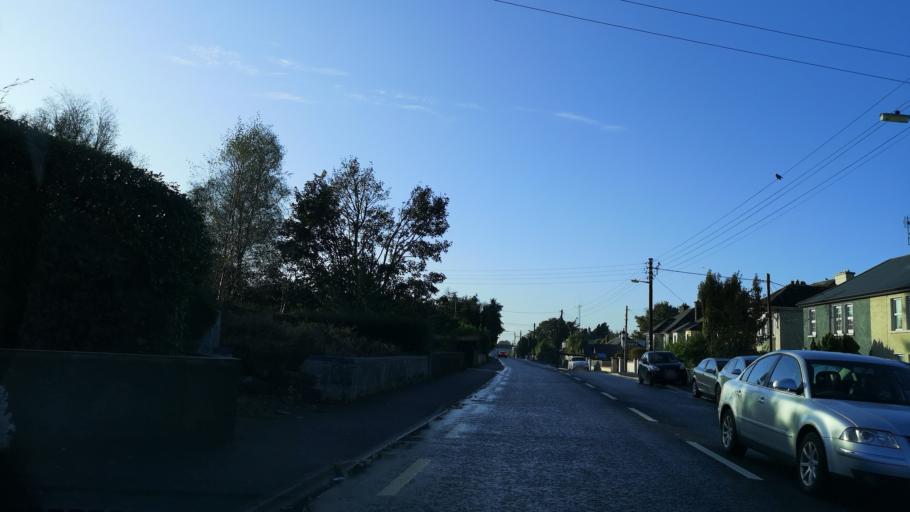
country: IE
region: Connaught
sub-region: Roscommon
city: Castlerea
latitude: 53.7650
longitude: -8.4796
